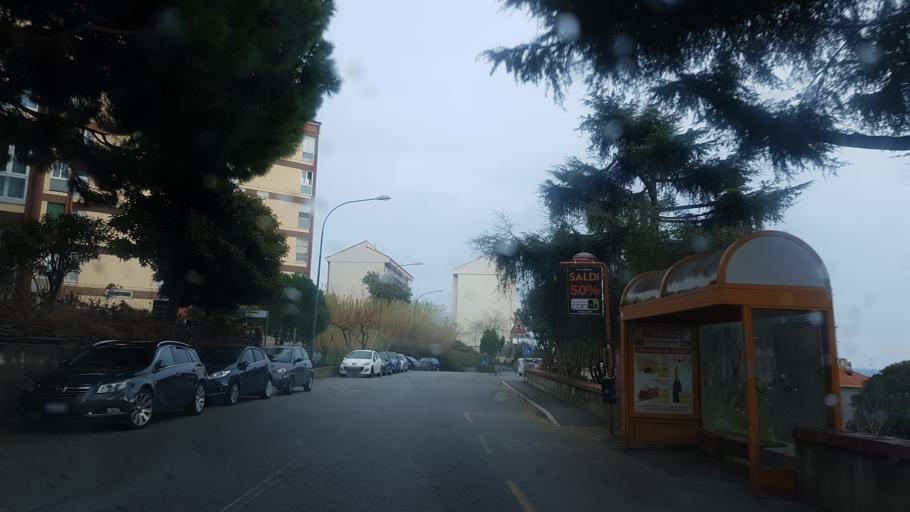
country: IT
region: Liguria
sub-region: Provincia di Savona
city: Savona
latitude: 44.3033
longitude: 8.4609
